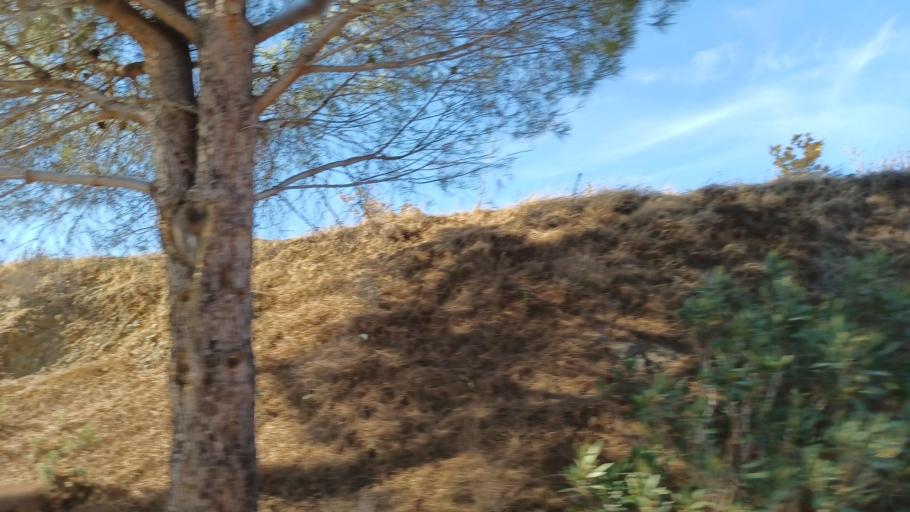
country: CY
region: Pafos
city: Polis
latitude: 34.9712
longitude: 32.4034
